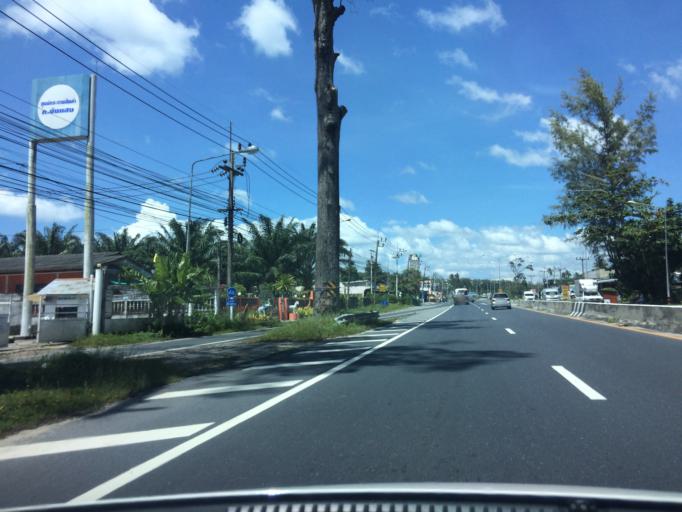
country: TH
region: Phangnga
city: Thai Mueang
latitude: 8.2318
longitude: 98.2976
